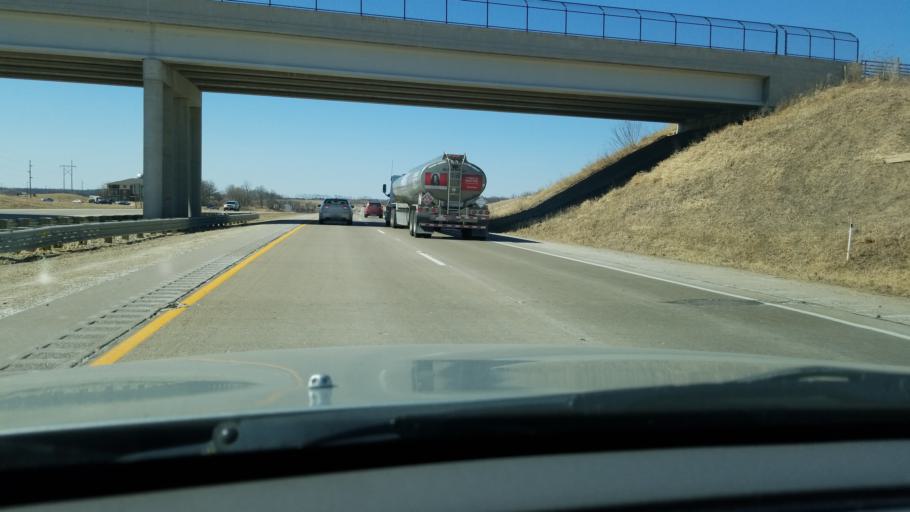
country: US
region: Wisconsin
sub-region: Dane County
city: Verona
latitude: 42.9732
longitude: -89.5329
